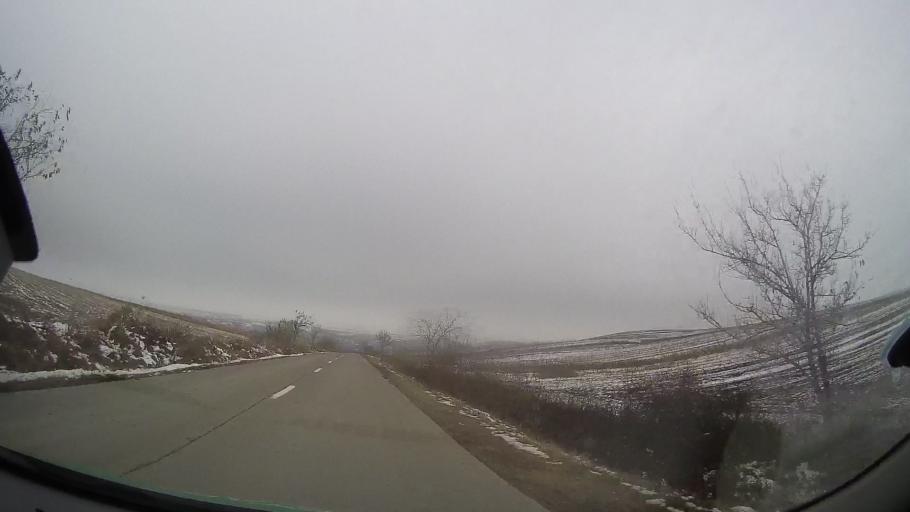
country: RO
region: Vaslui
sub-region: Comuna Ivesti
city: Ivesti
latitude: 46.1968
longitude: 27.5172
